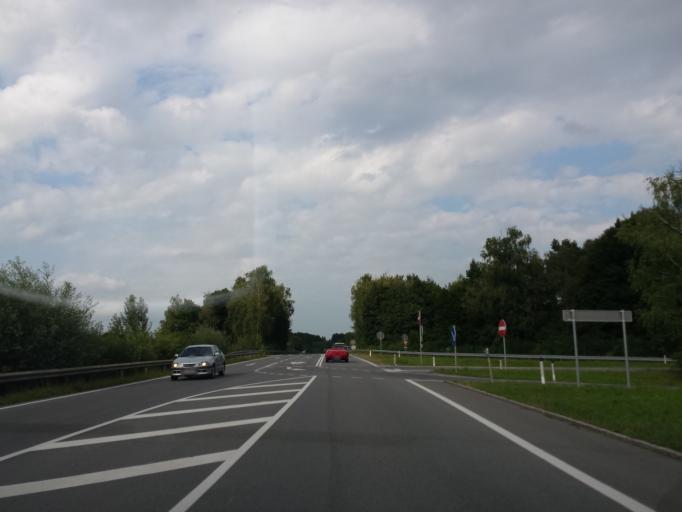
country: AT
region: Styria
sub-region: Politischer Bezirk Deutschlandsberg
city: Lannach
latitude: 46.9588
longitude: 15.3476
